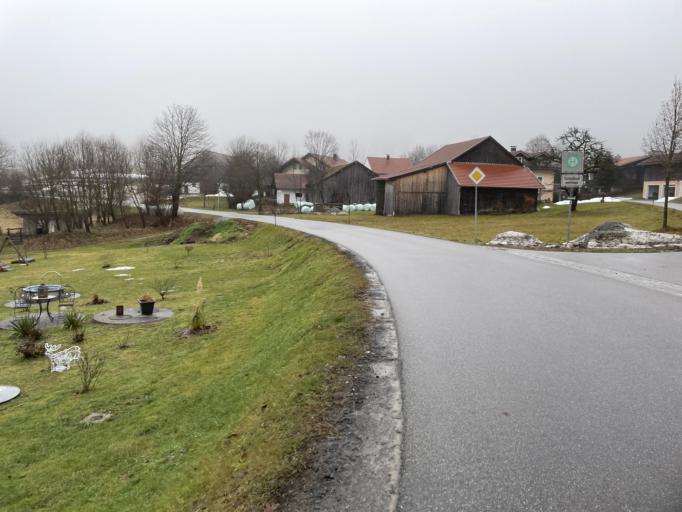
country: DE
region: Bavaria
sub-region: Lower Bavaria
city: Ruhmannsfelden
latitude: 48.9936
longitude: 13.0103
